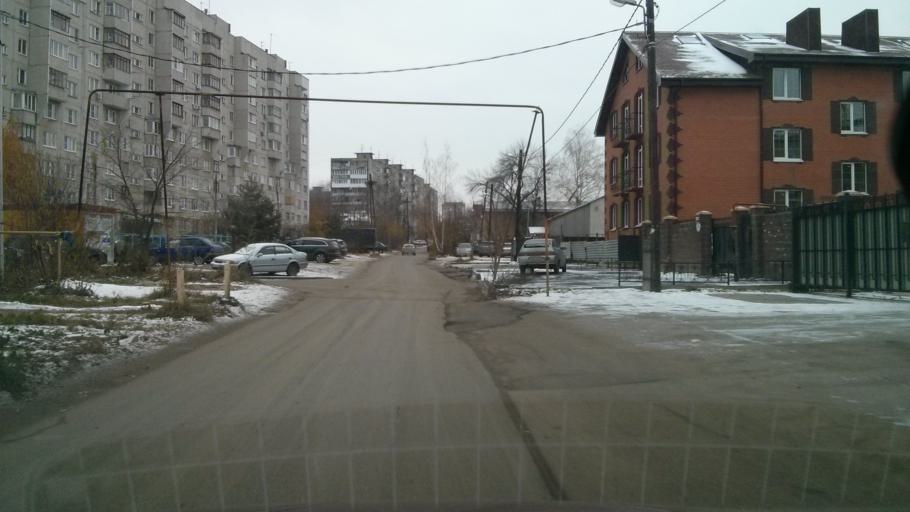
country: RU
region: Nizjnij Novgorod
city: Nizhniy Novgorod
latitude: 56.3055
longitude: 44.0424
